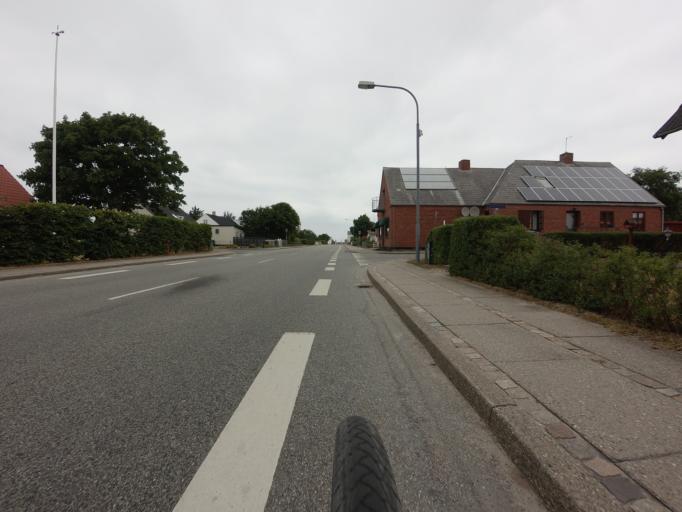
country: DK
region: North Denmark
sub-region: Laeso Kommune
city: Byrum
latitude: 57.2896
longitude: 10.9236
